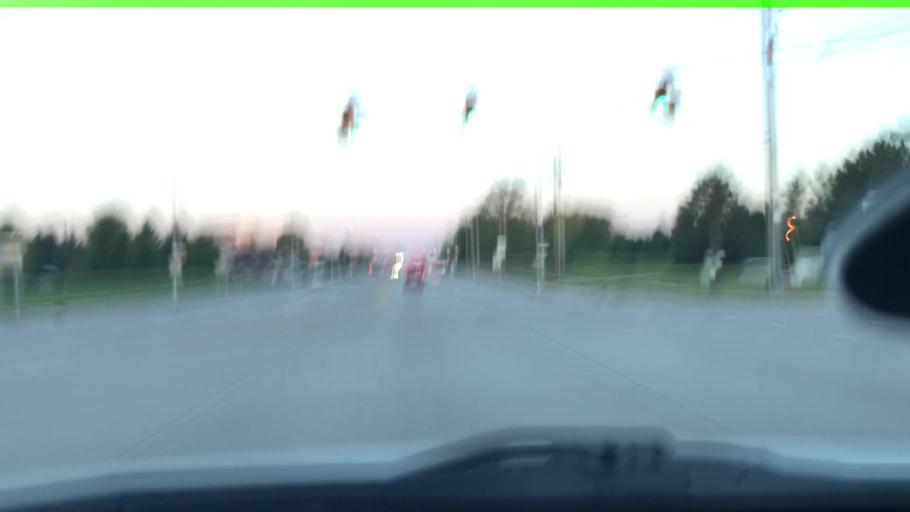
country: US
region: Ohio
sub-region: Franklin County
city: Hilliard
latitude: 40.0030
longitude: -83.1312
